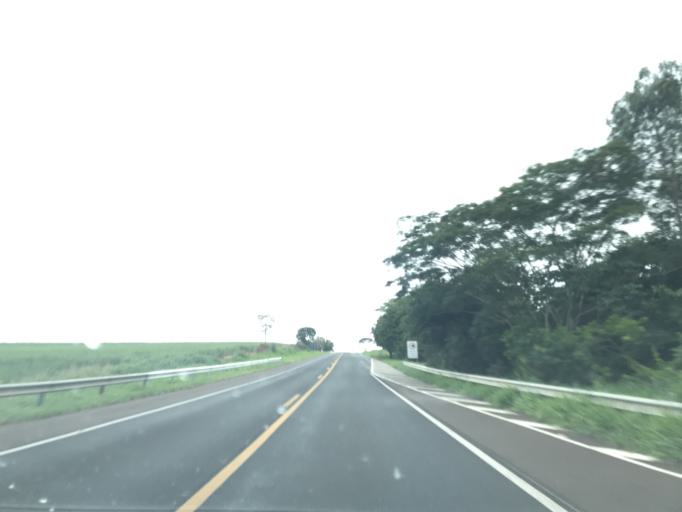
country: BR
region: Sao Paulo
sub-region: Penapolis
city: Penapolis
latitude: -21.4962
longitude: -50.2432
